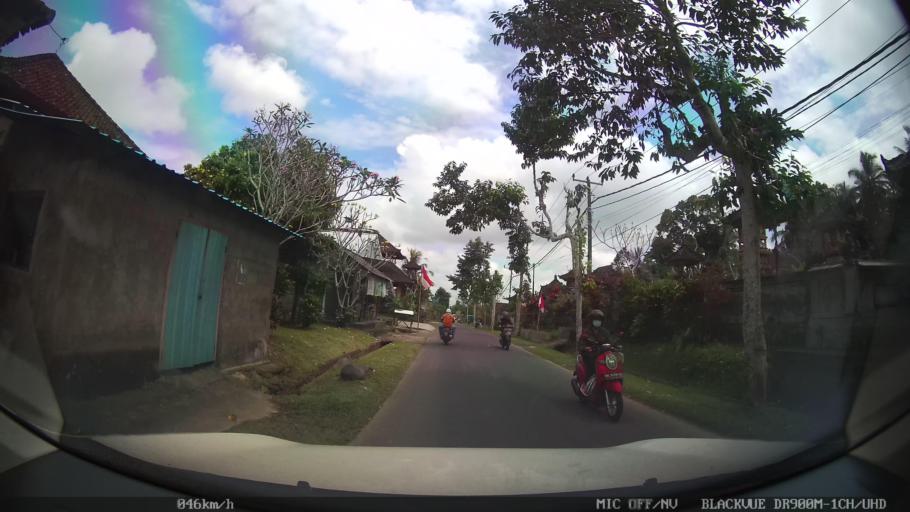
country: ID
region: Bali
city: Banjar Bebalang
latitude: -8.4753
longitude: 115.3768
